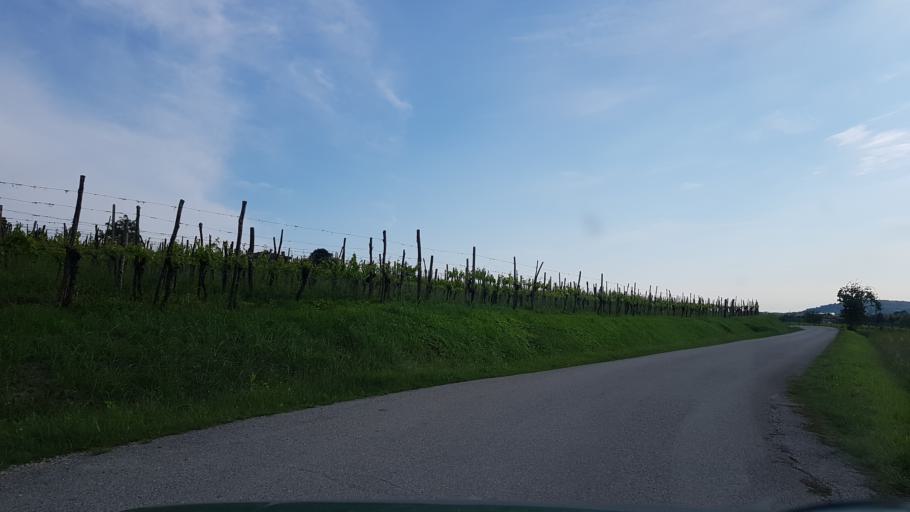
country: IT
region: Friuli Venezia Giulia
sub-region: Provincia di Gorizia
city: Cormons
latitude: 45.9554
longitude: 13.4858
